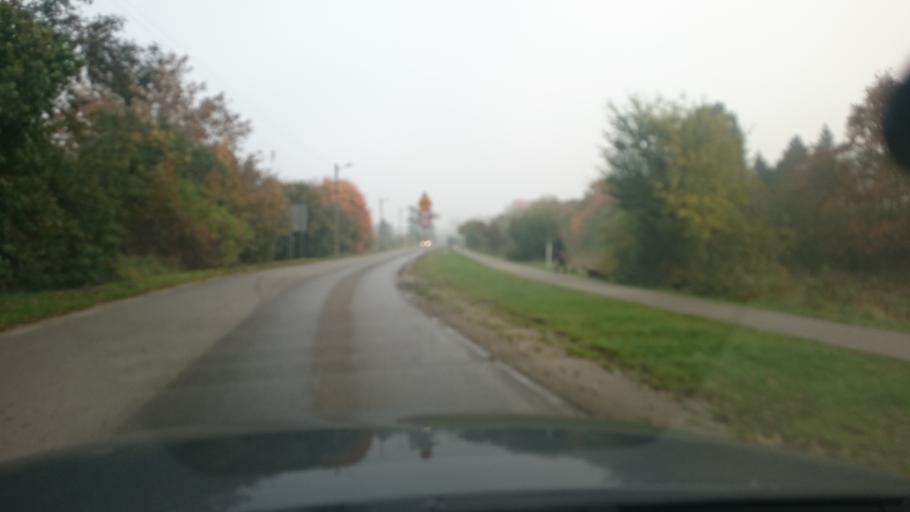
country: PL
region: Pomeranian Voivodeship
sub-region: Gdynia
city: Wielki Kack
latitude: 54.4663
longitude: 18.4974
